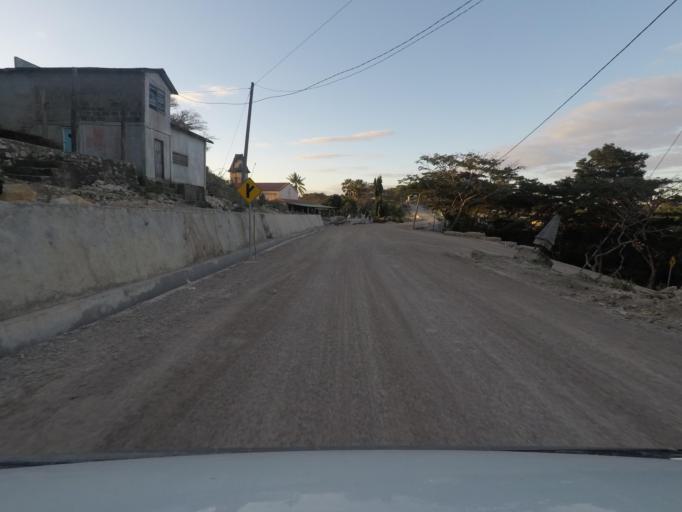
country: TL
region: Lautem
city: Lospalos
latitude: -8.3957
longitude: 127.2549
